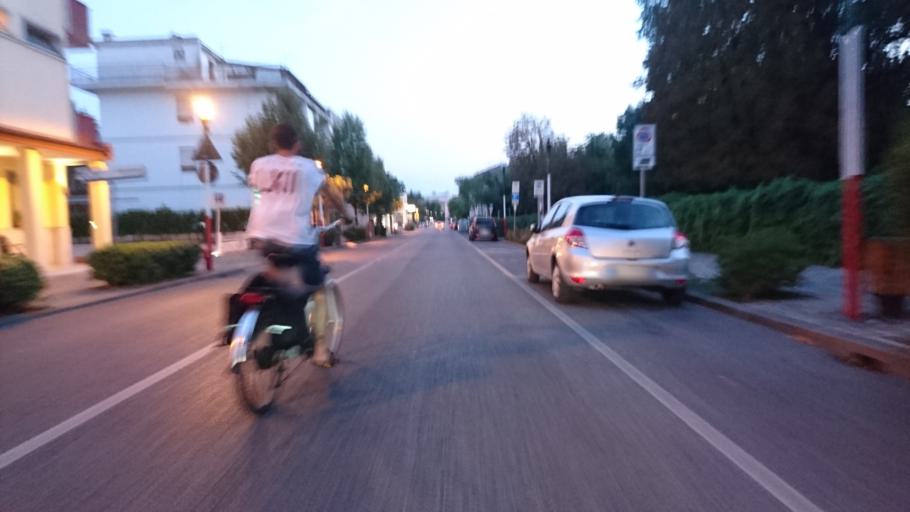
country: IT
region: Veneto
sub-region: Provincia di Padova
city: Abano Terme
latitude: 45.3583
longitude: 11.7879
